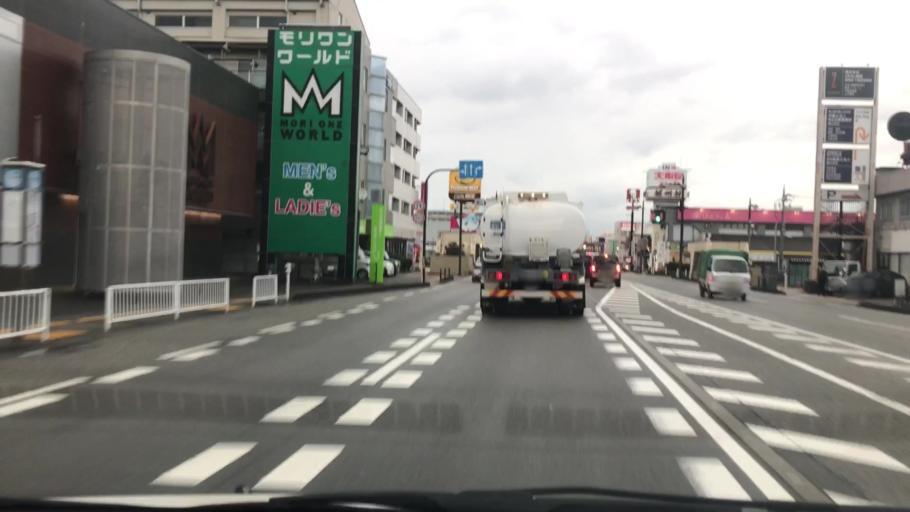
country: JP
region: Toyama
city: Toyama-shi
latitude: 36.6733
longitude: 137.2106
